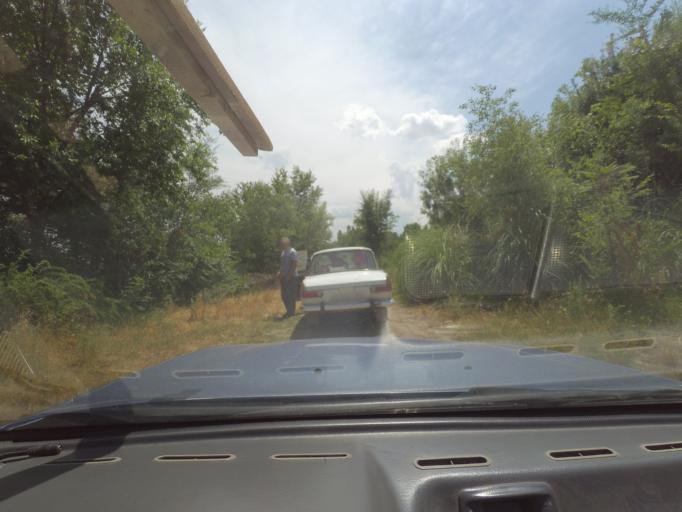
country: TJ
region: Viloyati Sughd
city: Buston
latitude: 40.5358
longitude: 69.0785
